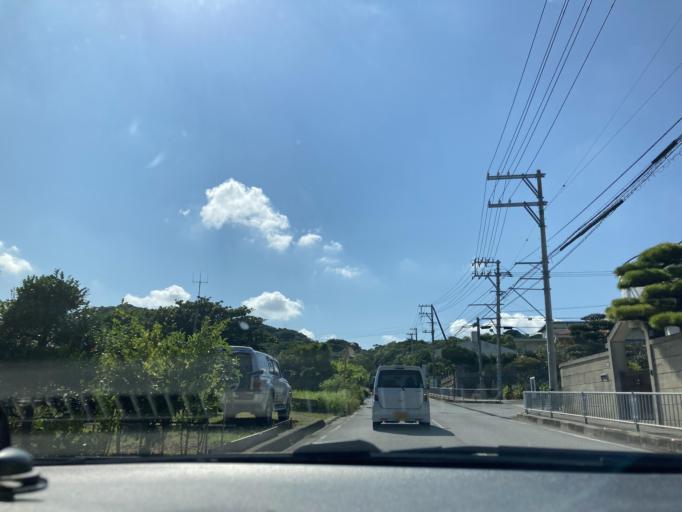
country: JP
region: Okinawa
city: Ginowan
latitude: 26.2227
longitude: 127.7510
